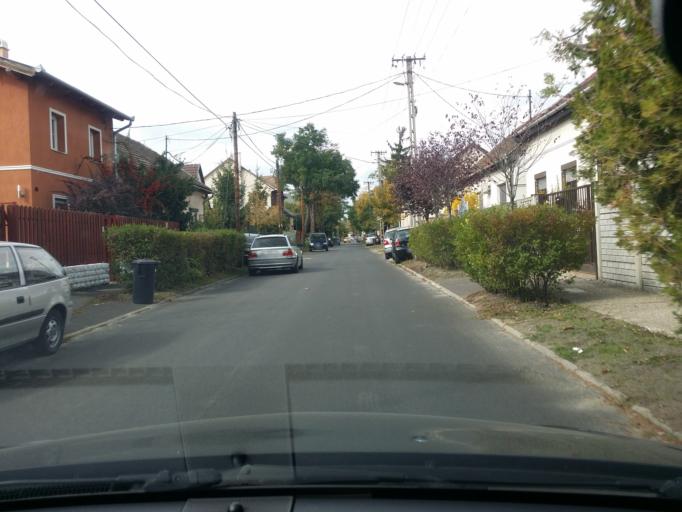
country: HU
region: Budapest
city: Budapest XIV. keruelet
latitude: 47.5370
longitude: 19.1287
